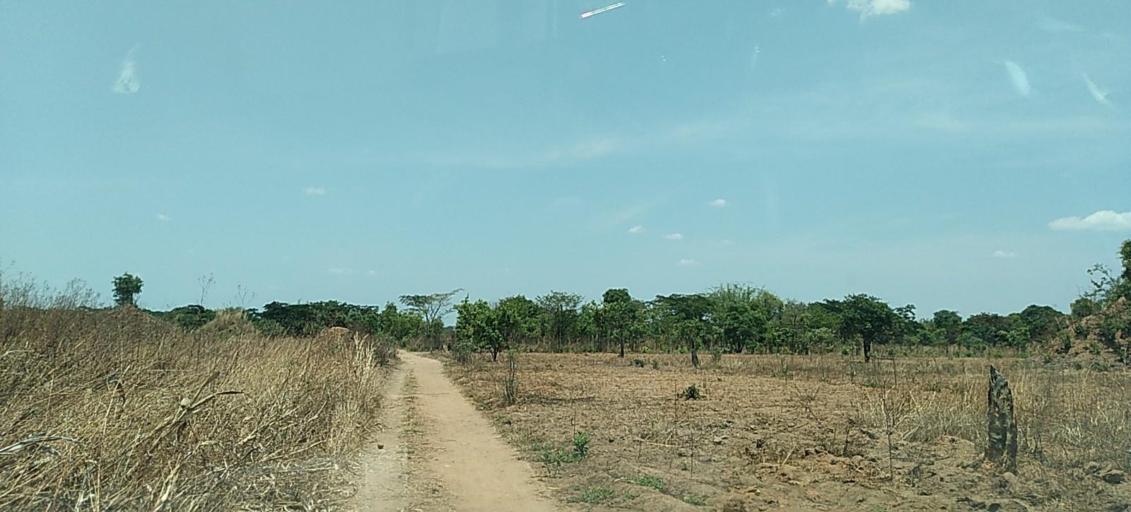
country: ZM
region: Copperbelt
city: Luanshya
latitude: -13.0619
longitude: 28.4088
